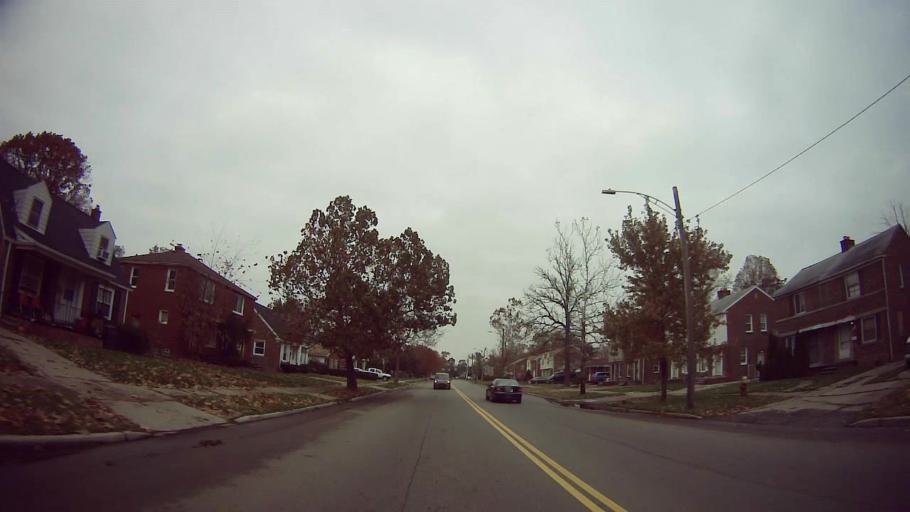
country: US
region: Michigan
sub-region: Wayne County
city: Dearborn Heights
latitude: 42.3483
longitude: -83.2356
